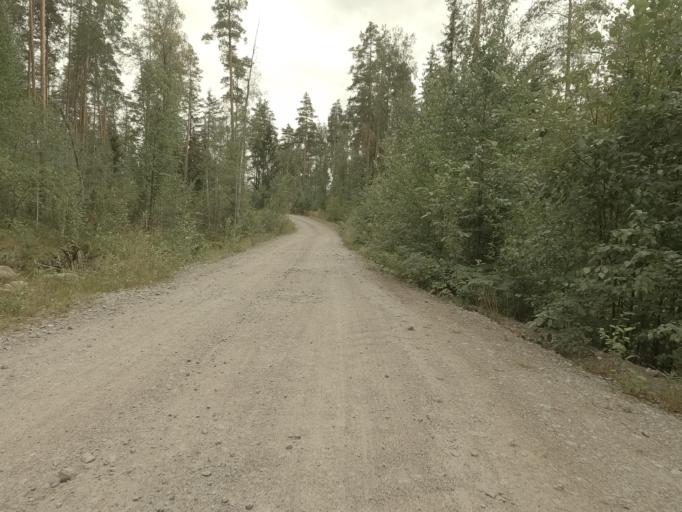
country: RU
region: Leningrad
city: Kamennogorsk
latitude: 60.9796
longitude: 29.1714
